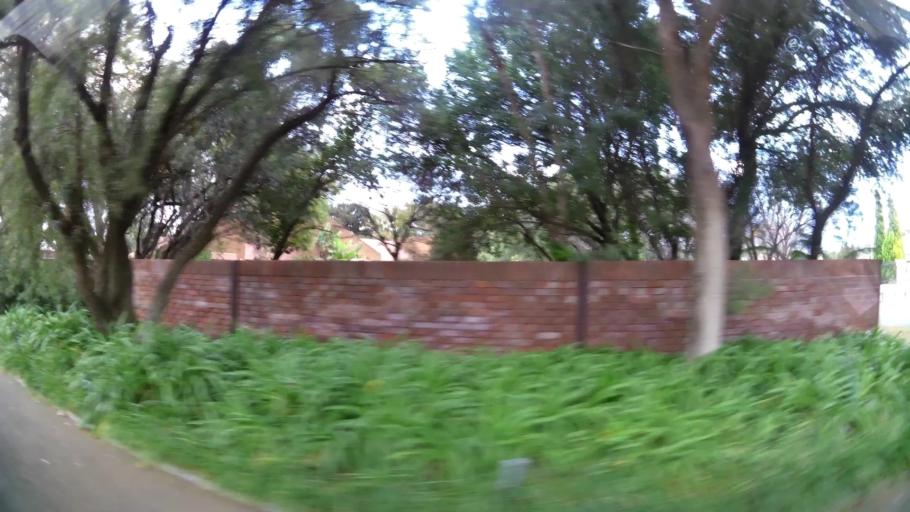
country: ZA
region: Orange Free State
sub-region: Lejweleputswa District Municipality
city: Welkom
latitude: -27.9558
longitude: 26.7394
